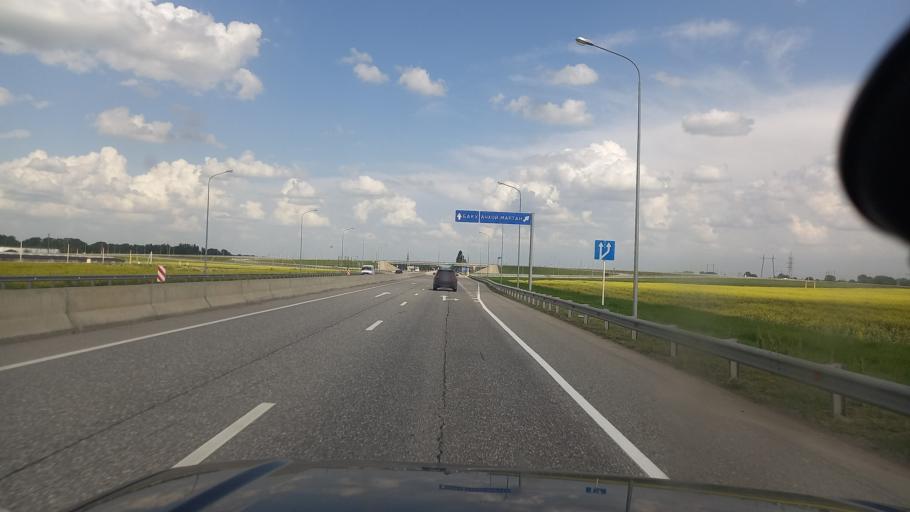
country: RU
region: Chechnya
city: Samashki
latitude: 43.2439
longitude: 45.2834
